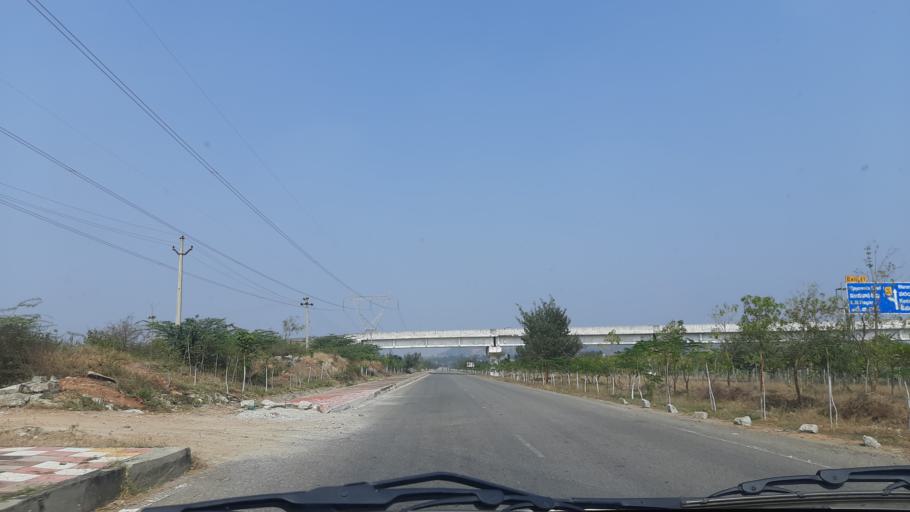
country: IN
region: Telangana
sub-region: Rangareddi
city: Lal Bahadur Nagar
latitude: 17.3066
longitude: 78.6549
